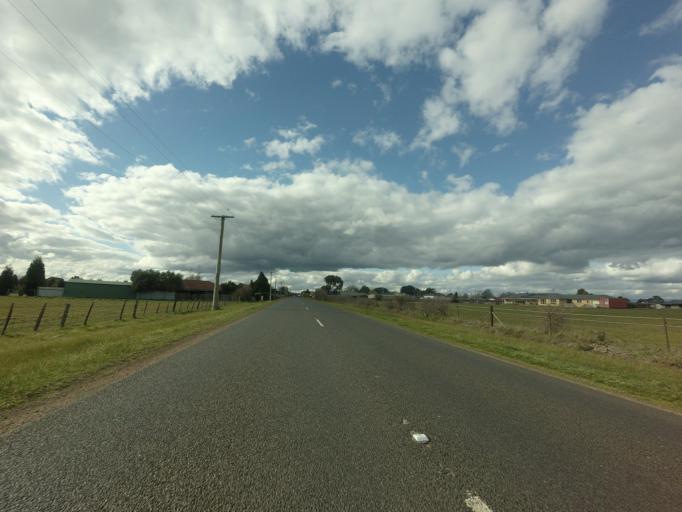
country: AU
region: Tasmania
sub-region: Northern Midlands
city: Longford
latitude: -41.6114
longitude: 147.1146
